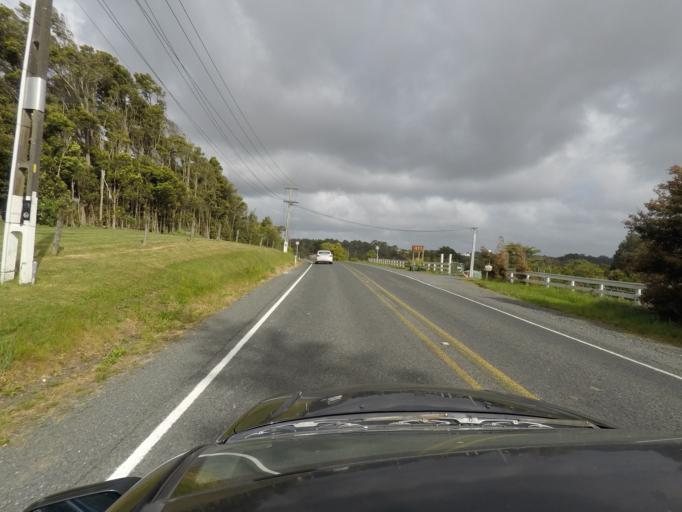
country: NZ
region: Auckland
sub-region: Auckland
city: Pakuranga
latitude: -36.9348
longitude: 174.9393
